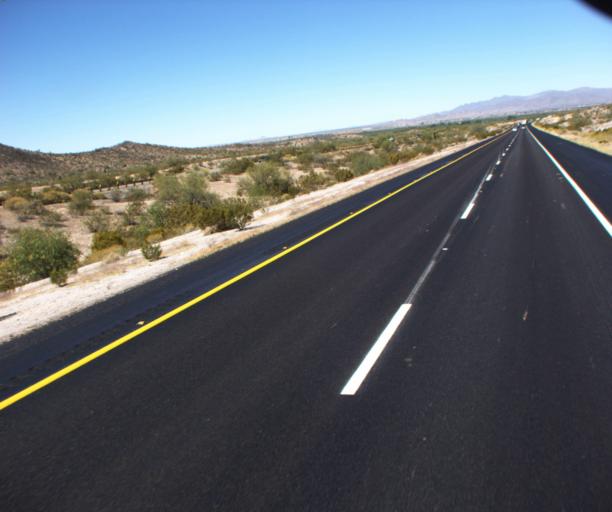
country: US
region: Arizona
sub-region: Maricopa County
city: Buckeye
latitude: 33.3050
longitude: -112.6258
